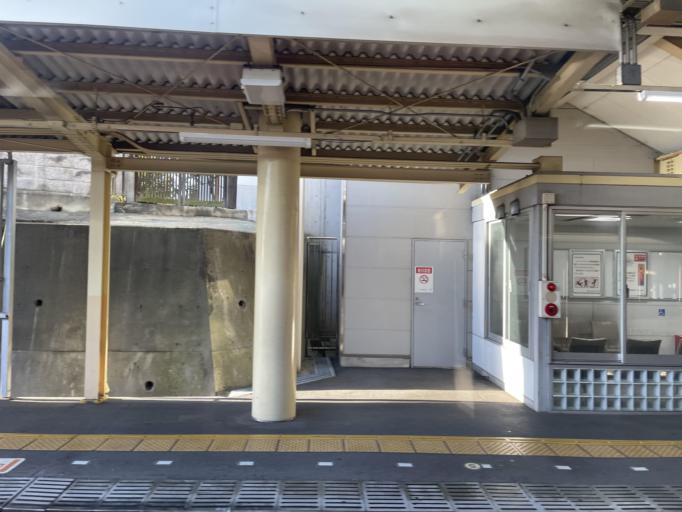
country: JP
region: Osaka
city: Kashihara
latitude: 34.5717
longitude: 135.6152
